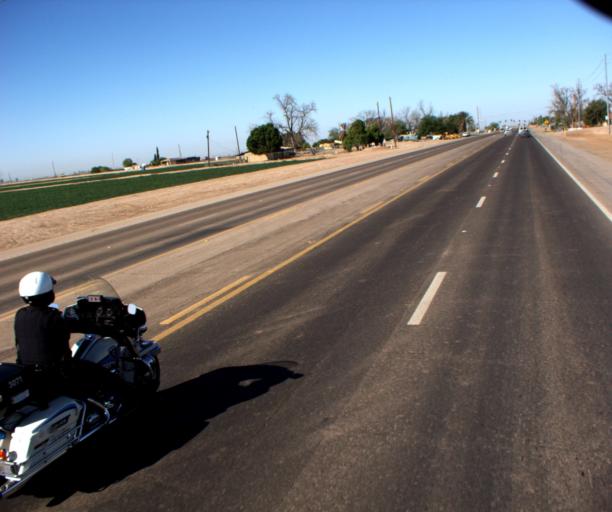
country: US
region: Arizona
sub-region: Yuma County
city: Somerton
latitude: 32.5968
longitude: -114.7309
